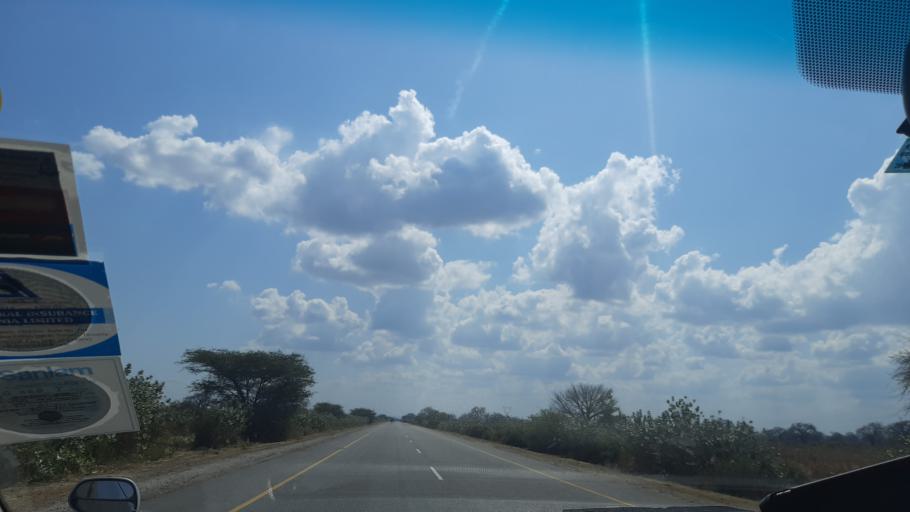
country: TZ
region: Singida
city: Kintinku
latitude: -5.9301
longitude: 35.2764
